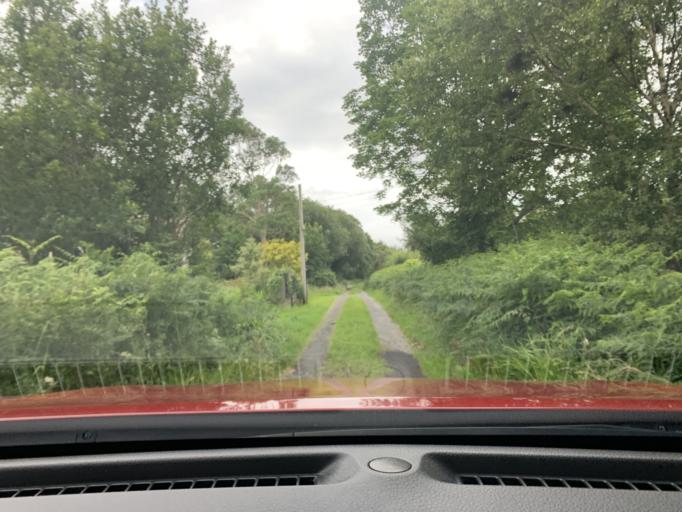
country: IE
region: Connaught
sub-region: County Leitrim
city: Kinlough
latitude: 54.4568
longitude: -8.3577
